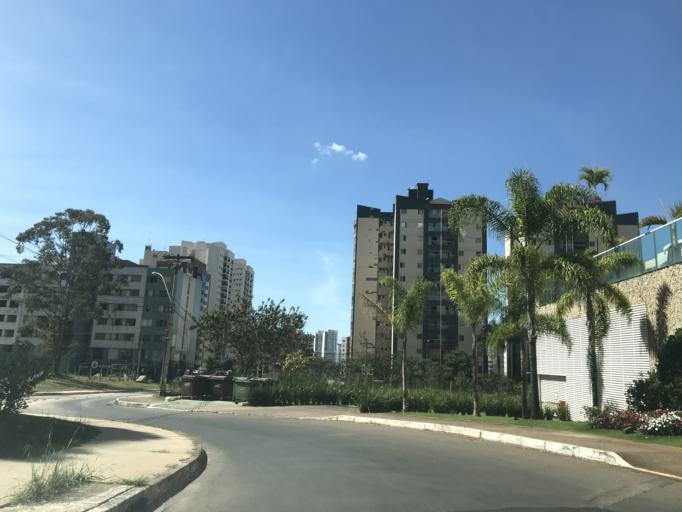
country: BR
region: Federal District
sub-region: Brasilia
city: Brasilia
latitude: -15.8360
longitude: -48.0310
